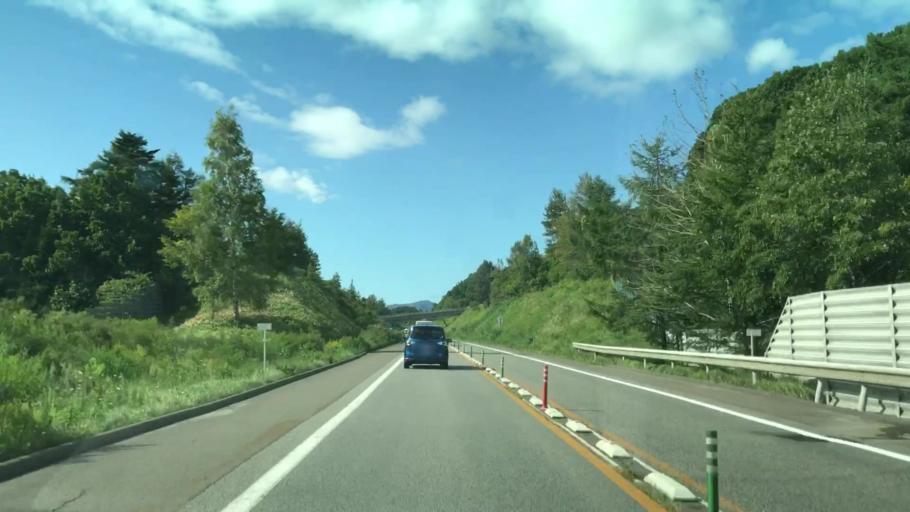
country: JP
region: Hokkaido
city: Date
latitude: 42.4363
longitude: 140.9213
